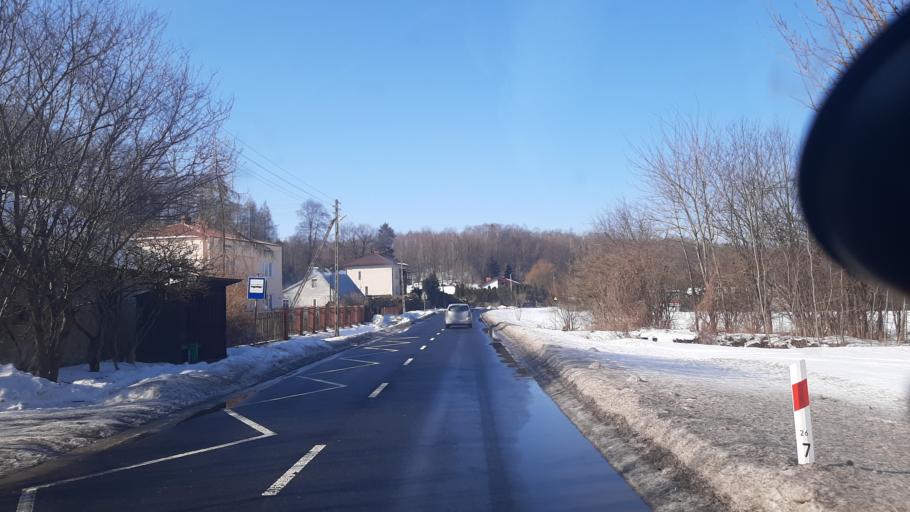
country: PL
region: Lublin Voivodeship
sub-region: Powiat pulawski
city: Wawolnica
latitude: 51.2837
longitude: 22.1719
